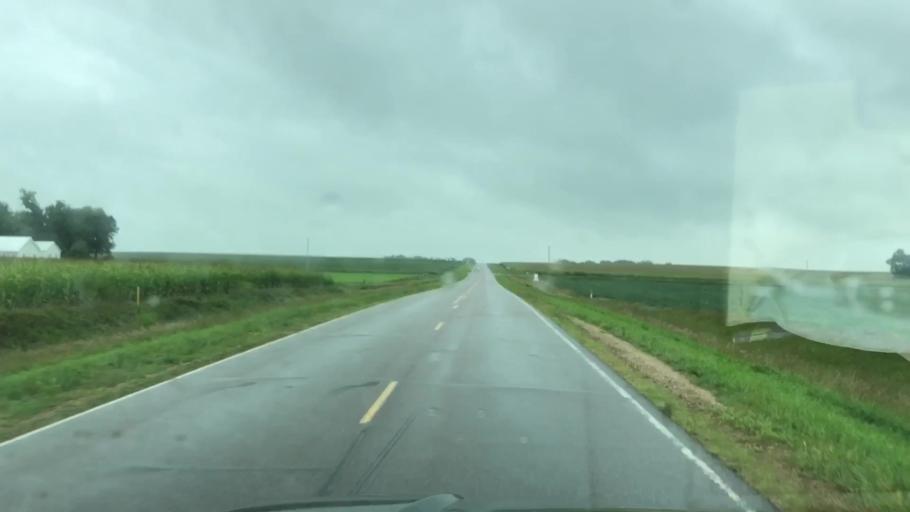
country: US
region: Iowa
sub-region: O'Brien County
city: Sanborn
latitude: 43.1962
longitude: -95.7231
